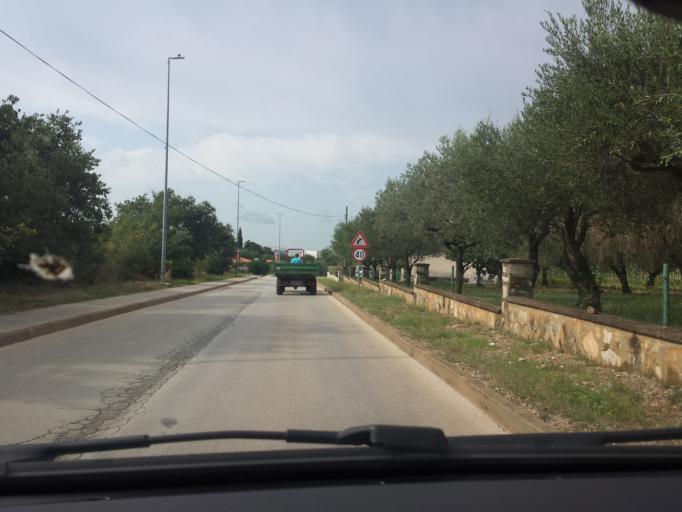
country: HR
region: Istarska
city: Galizana
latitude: 44.9263
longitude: 13.8663
